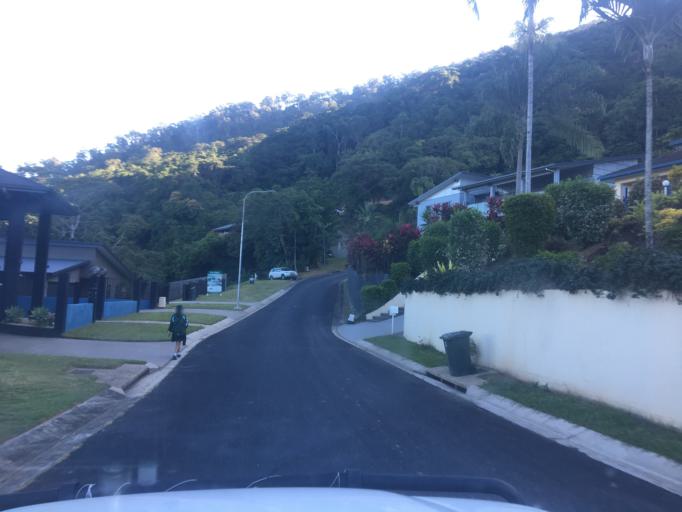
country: AU
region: Queensland
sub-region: Cairns
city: Woree
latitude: -16.9350
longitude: 145.7224
